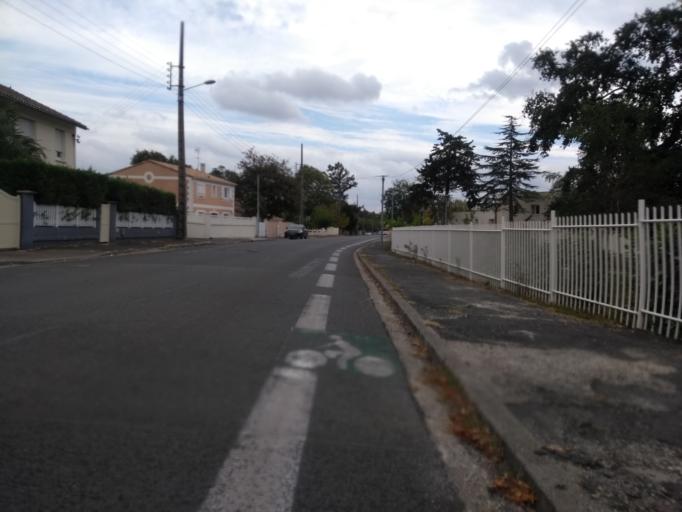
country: FR
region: Aquitaine
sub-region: Departement de la Gironde
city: Pessac
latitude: 44.8246
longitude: -0.6622
